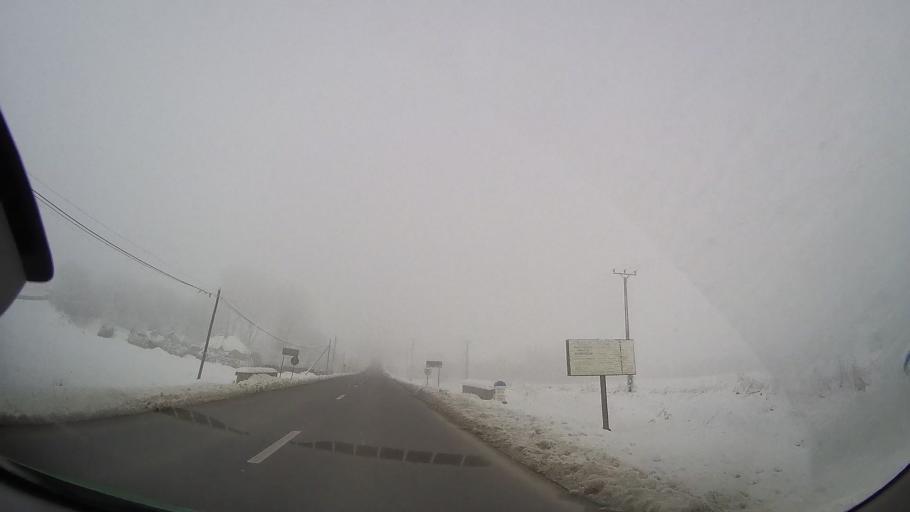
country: RO
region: Iasi
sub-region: Comuna Stolniceni-Prajescu
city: Stolniceni-Prajescu
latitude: 47.1921
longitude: 26.7374
